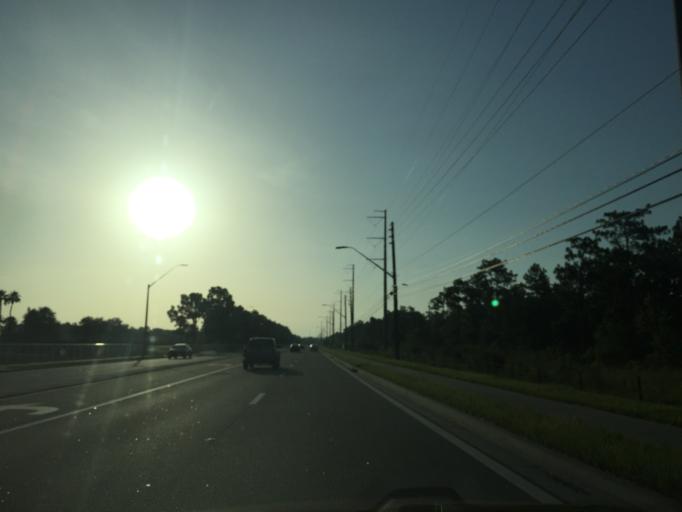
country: US
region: Florida
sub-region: Orange County
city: Alafaya
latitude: 28.5108
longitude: -81.1810
